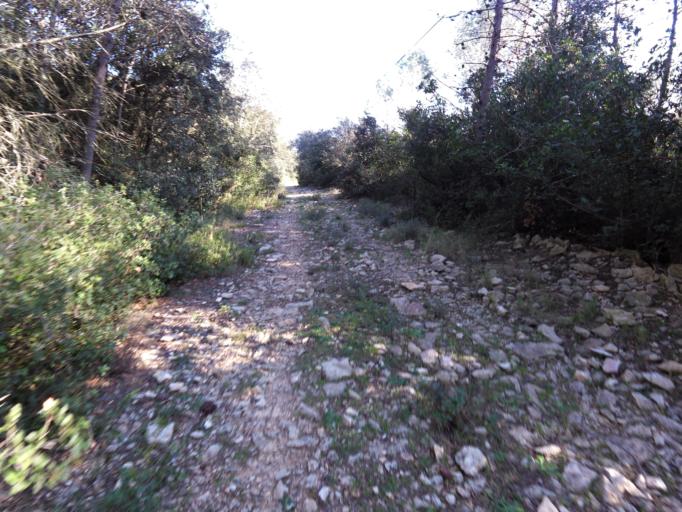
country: FR
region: Languedoc-Roussillon
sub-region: Departement du Gard
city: Congenies
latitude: 43.7601
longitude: 4.1673
